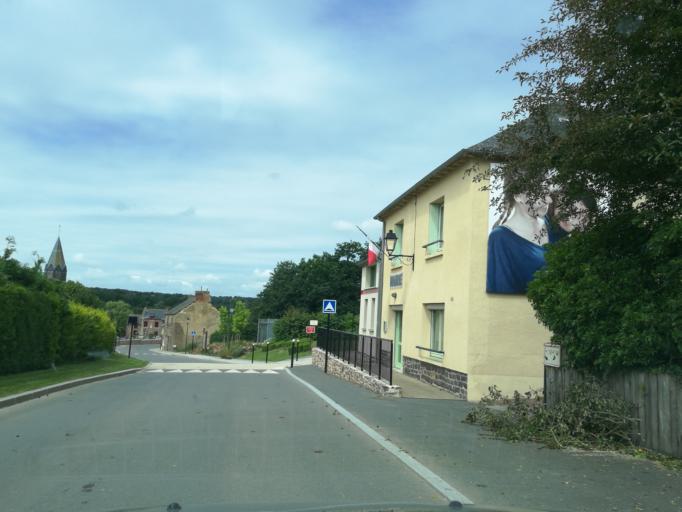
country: FR
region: Brittany
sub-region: Departement d'Ille-et-Vilaine
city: Bedee
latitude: 48.1624
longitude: -1.9780
